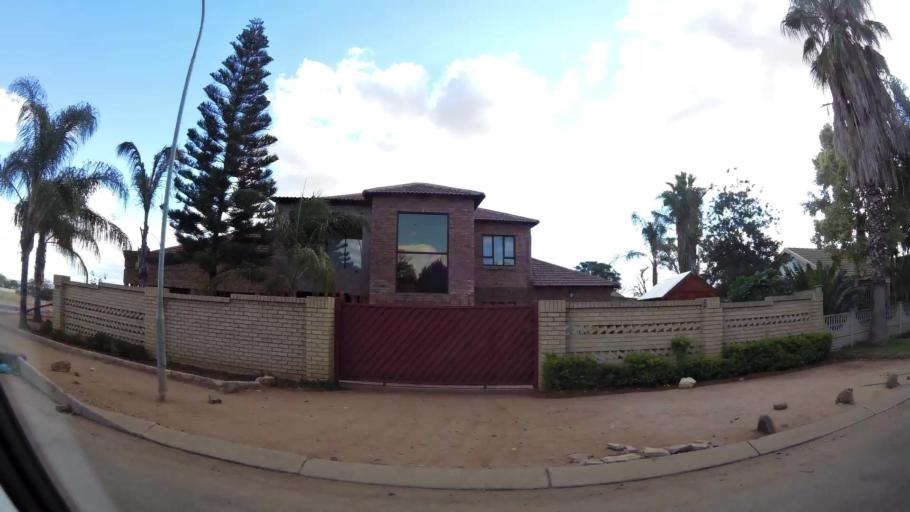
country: ZA
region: Limpopo
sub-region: Capricorn District Municipality
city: Polokwane
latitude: -23.9120
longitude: 29.4986
